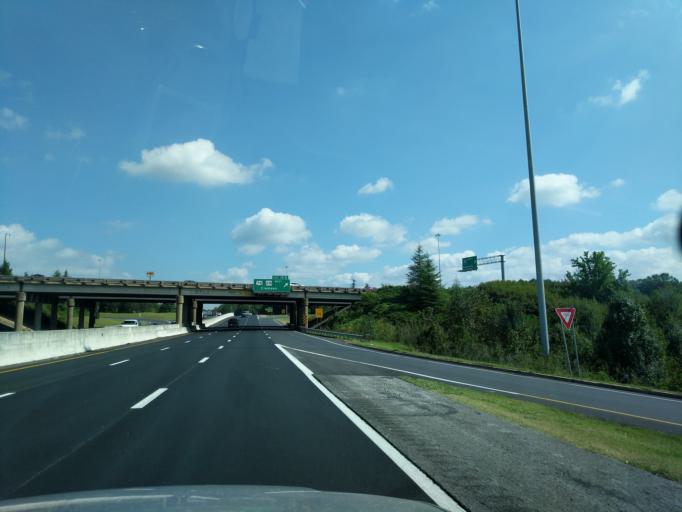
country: US
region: South Carolina
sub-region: Anderson County
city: Northlake
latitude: 34.5730
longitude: -82.7158
